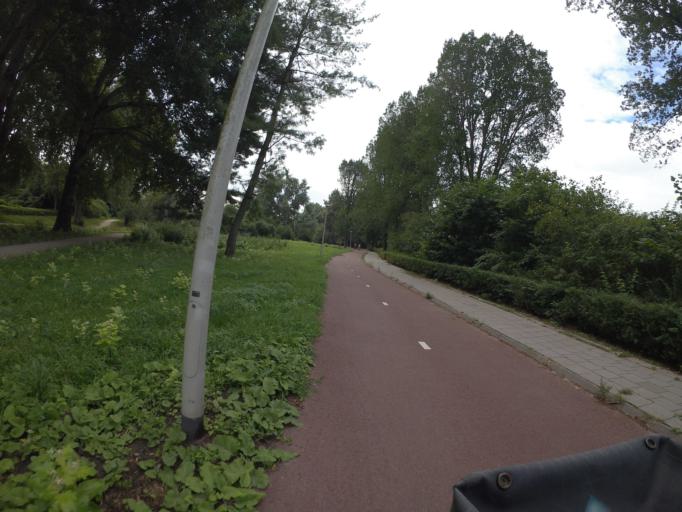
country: NL
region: North Brabant
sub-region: Roosendaal
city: Roosendaal
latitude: 51.5128
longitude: 4.4548
